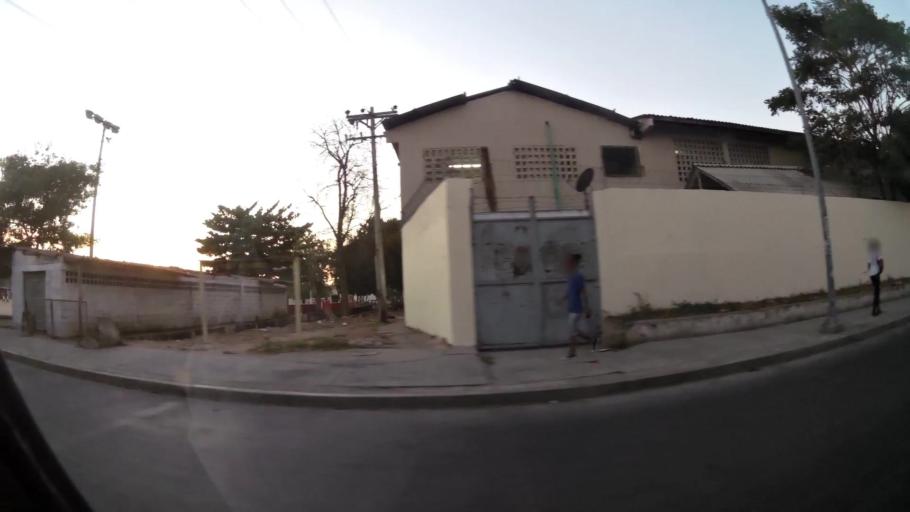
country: CO
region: Atlantico
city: Barranquilla
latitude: 10.9430
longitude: -74.7775
